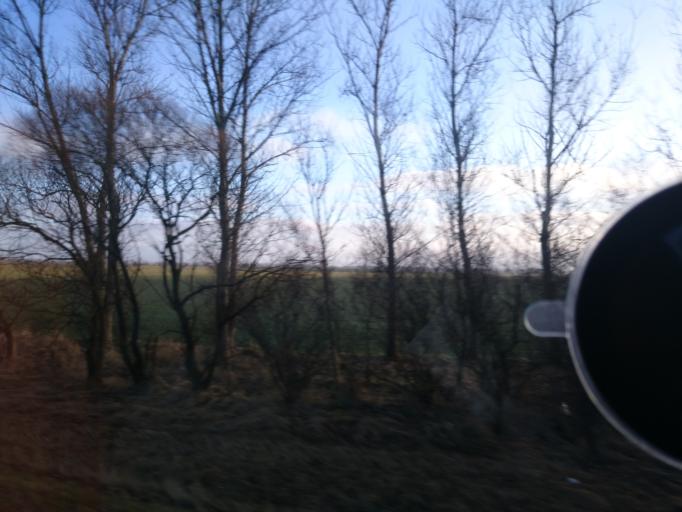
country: DE
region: Brandenburg
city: Fehrbellin
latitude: 52.7805
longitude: 12.8042
